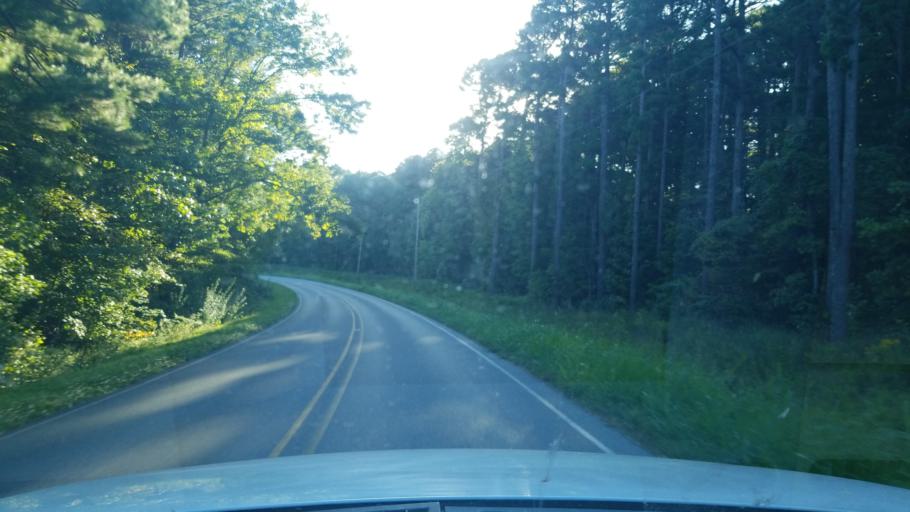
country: US
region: Illinois
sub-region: Hardin County
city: Elizabethtown
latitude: 37.5769
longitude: -88.3858
